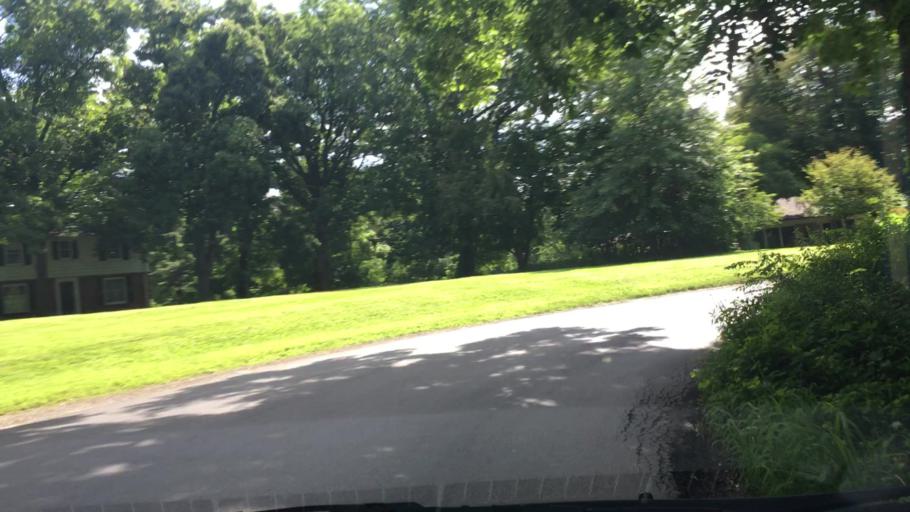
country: US
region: Iowa
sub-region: Johnson County
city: Iowa City
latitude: 41.6907
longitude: -91.5341
